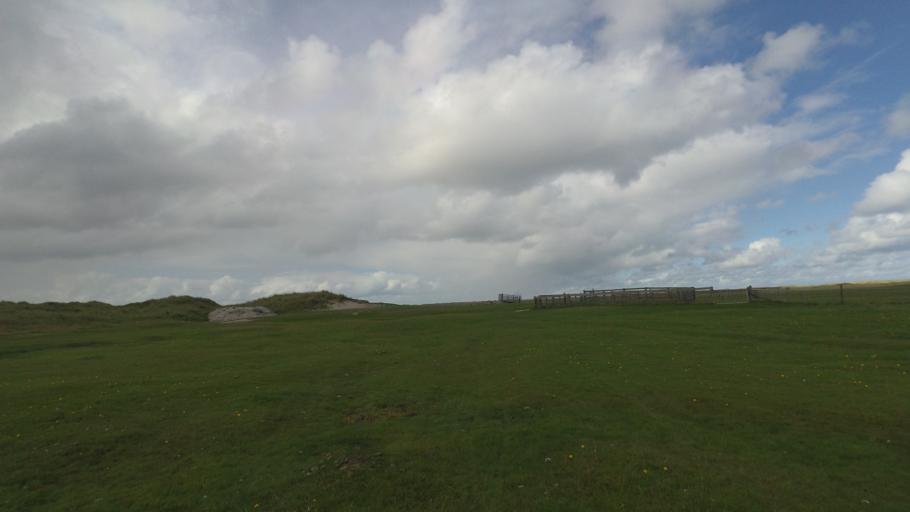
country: NL
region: Friesland
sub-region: Gemeente Ameland
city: Nes
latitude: 53.4503
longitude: 5.8603
